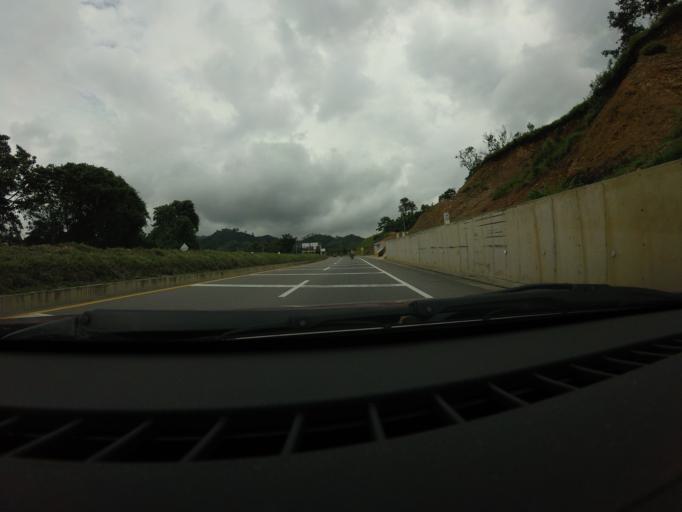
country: CO
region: Cundinamarca
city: San Francisco
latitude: 4.9776
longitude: -74.3095
